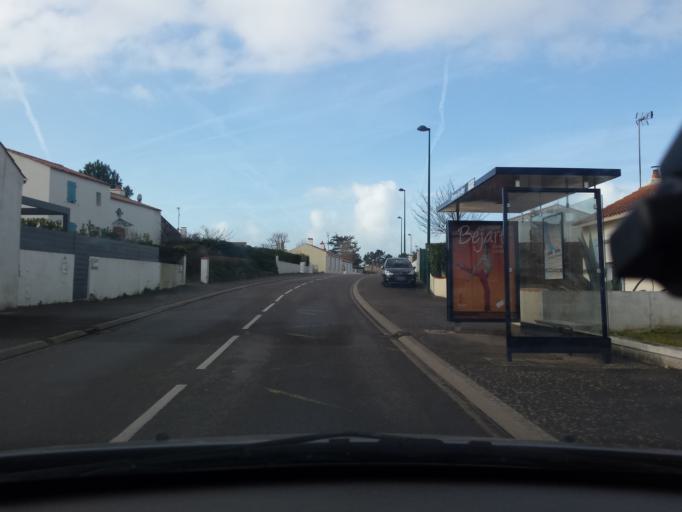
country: FR
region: Pays de la Loire
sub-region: Departement de la Vendee
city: Olonne-sur-Mer
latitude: 46.5478
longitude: -1.8007
